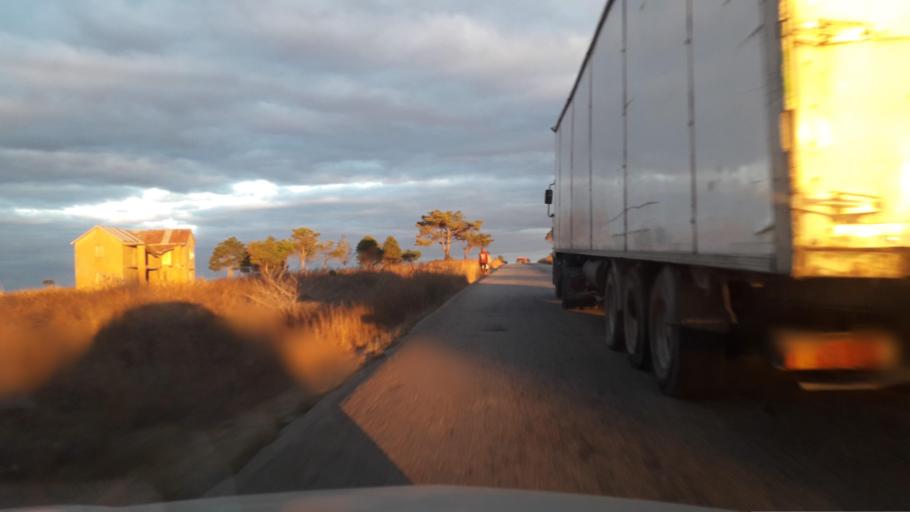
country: MG
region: Analamanga
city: Ankazobe
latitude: -17.8845
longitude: 47.0827
